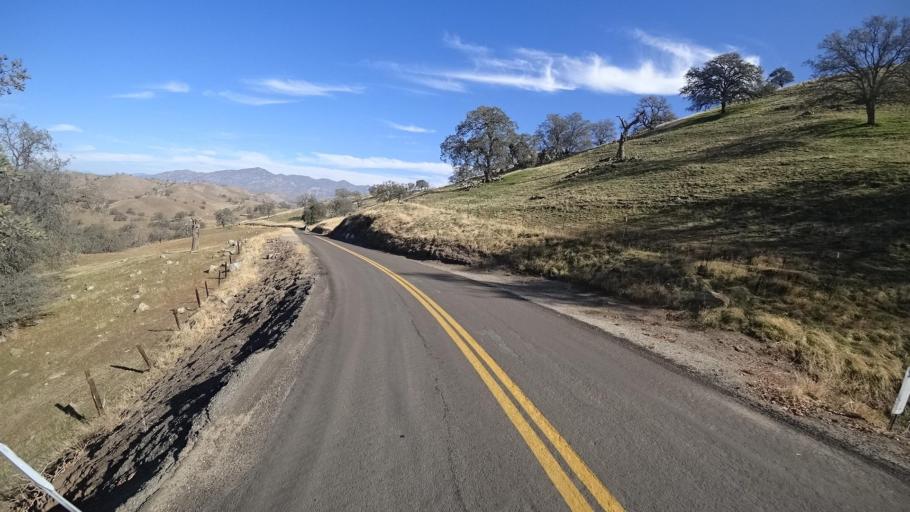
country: US
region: California
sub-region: Tulare County
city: Richgrove
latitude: 35.6953
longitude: -118.8616
